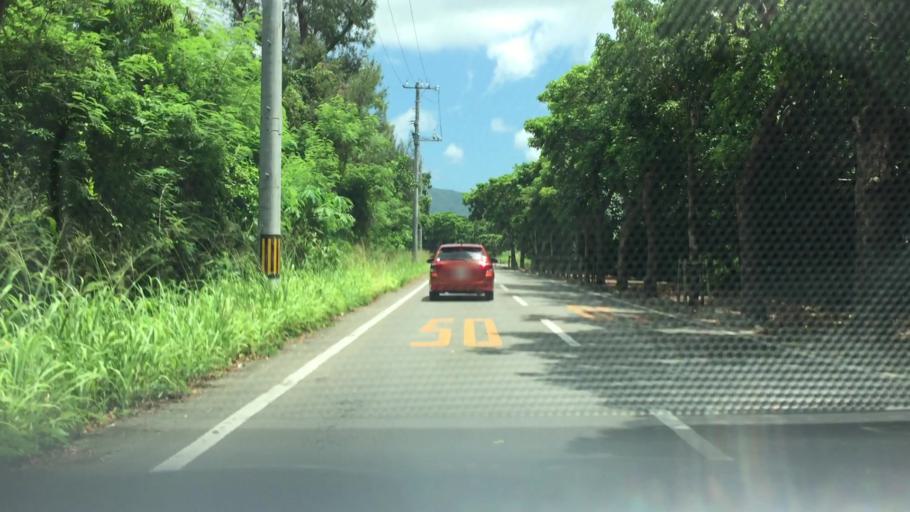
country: JP
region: Okinawa
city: Ishigaki
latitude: 24.3878
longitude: 124.1397
